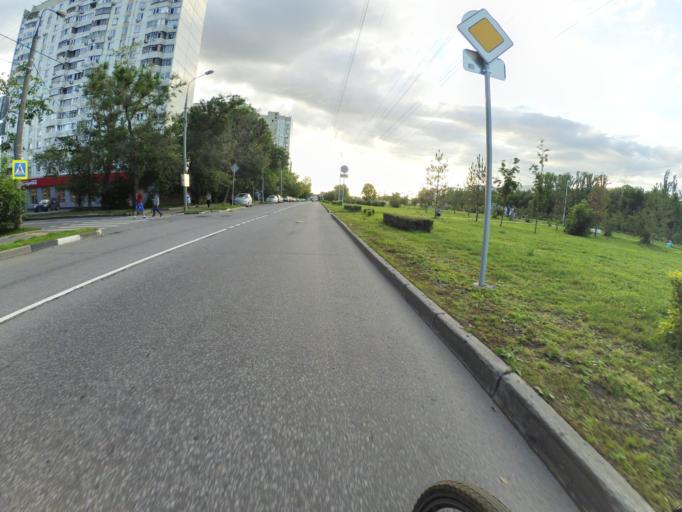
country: RU
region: Moscow
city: Pokrovskoye-Streshnevo
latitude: 55.8350
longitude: 37.4515
